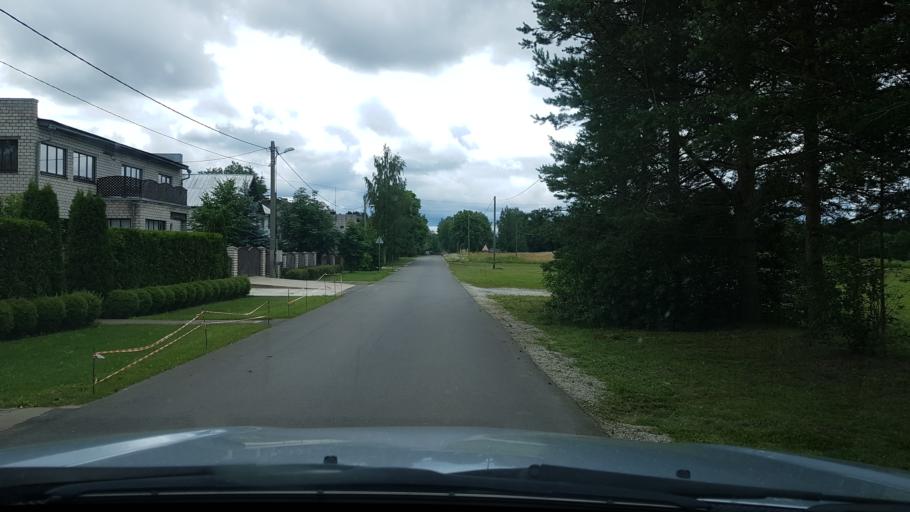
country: EE
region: Ida-Virumaa
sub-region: Sillamaee linn
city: Sillamae
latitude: 59.3704
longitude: 27.7617
